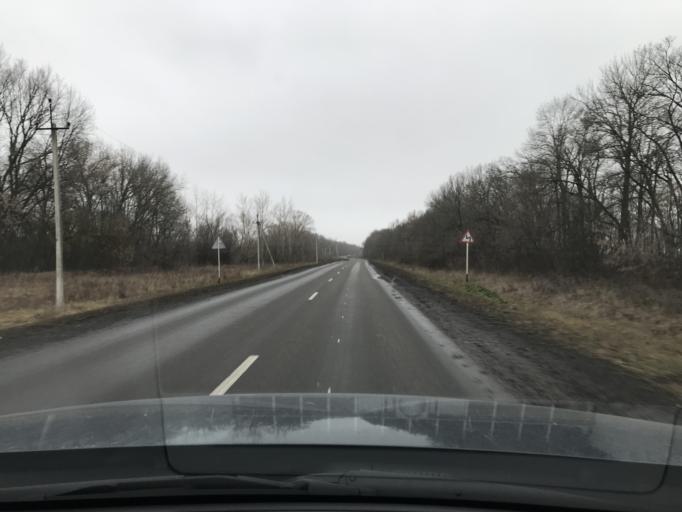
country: RU
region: Penza
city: Zemetchino
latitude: 53.5273
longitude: 42.6555
